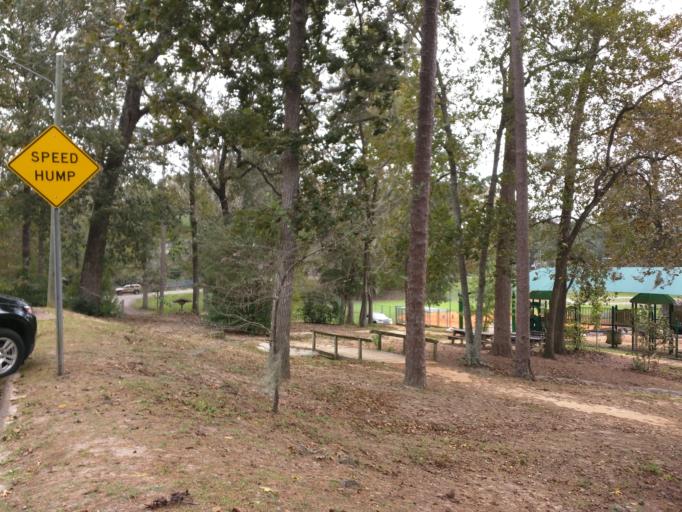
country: US
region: Florida
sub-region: Leon County
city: Tallahassee
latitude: 30.4531
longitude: -84.2742
